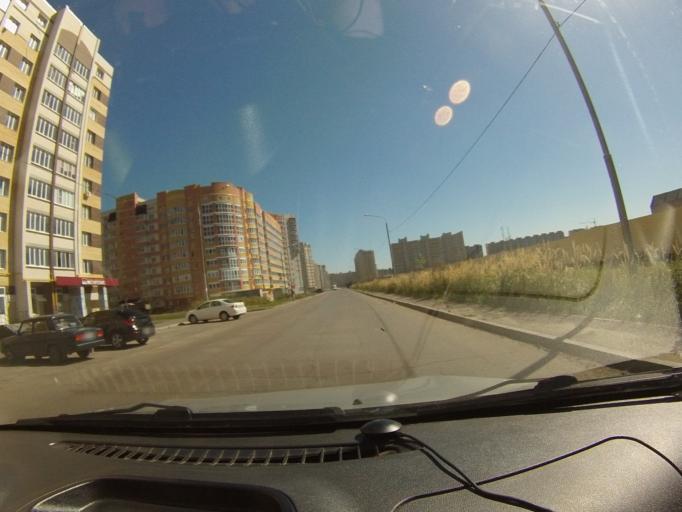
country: RU
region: Tambov
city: Tambov
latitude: 52.7719
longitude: 41.3925
